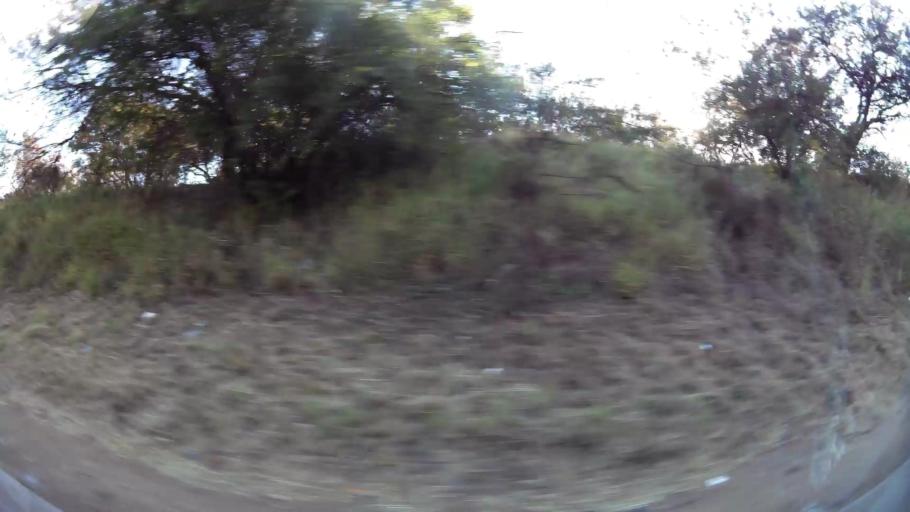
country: ZA
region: Gauteng
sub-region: City of Tshwane Metropolitan Municipality
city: Pretoria
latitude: -25.7569
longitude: 28.1333
